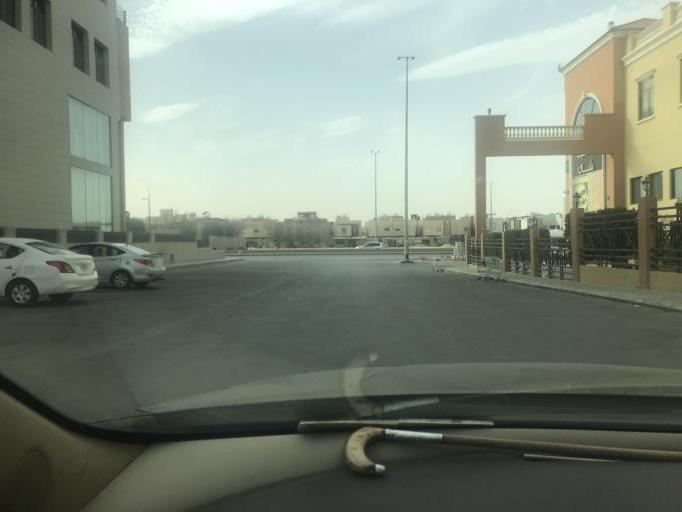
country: SA
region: Ar Riyad
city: Riyadh
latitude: 24.8087
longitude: 46.6681
